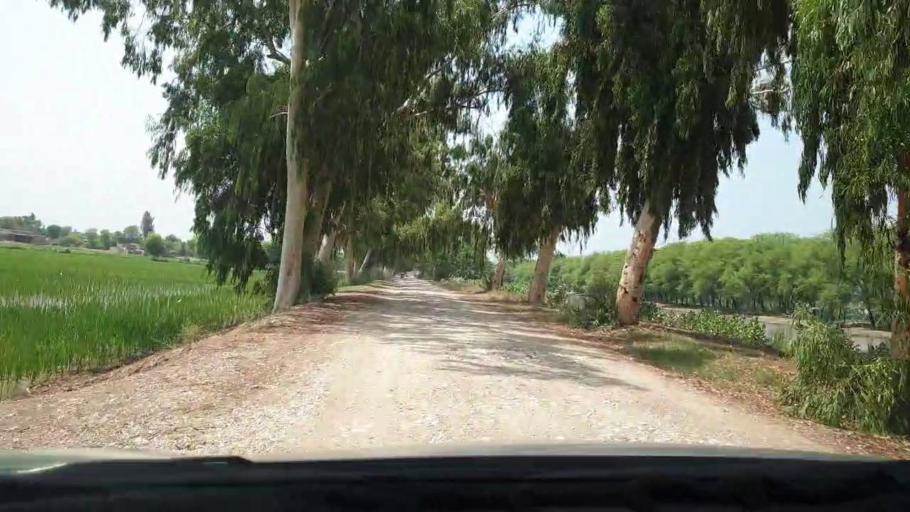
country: PK
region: Sindh
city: New Badah
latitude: 27.2991
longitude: 68.0890
